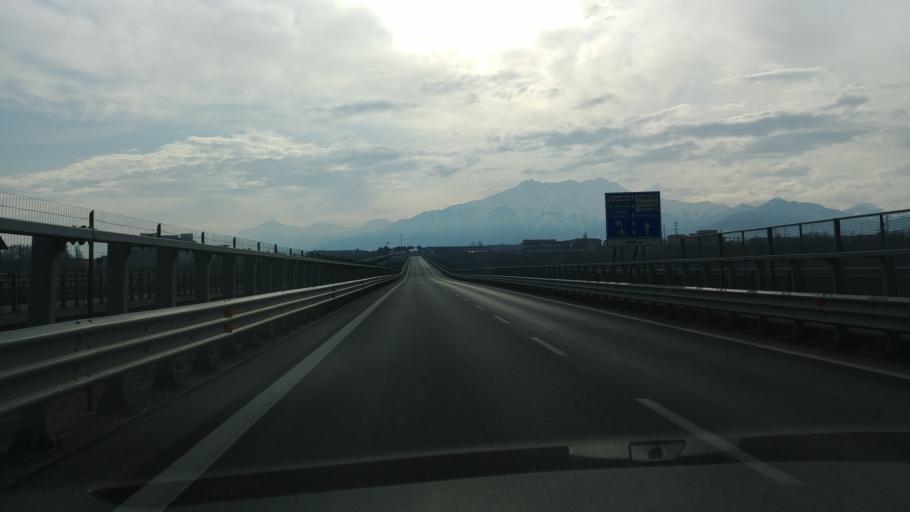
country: IT
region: Piedmont
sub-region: Provincia di Cuneo
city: Cuneo
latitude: 44.3866
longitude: 7.5215
